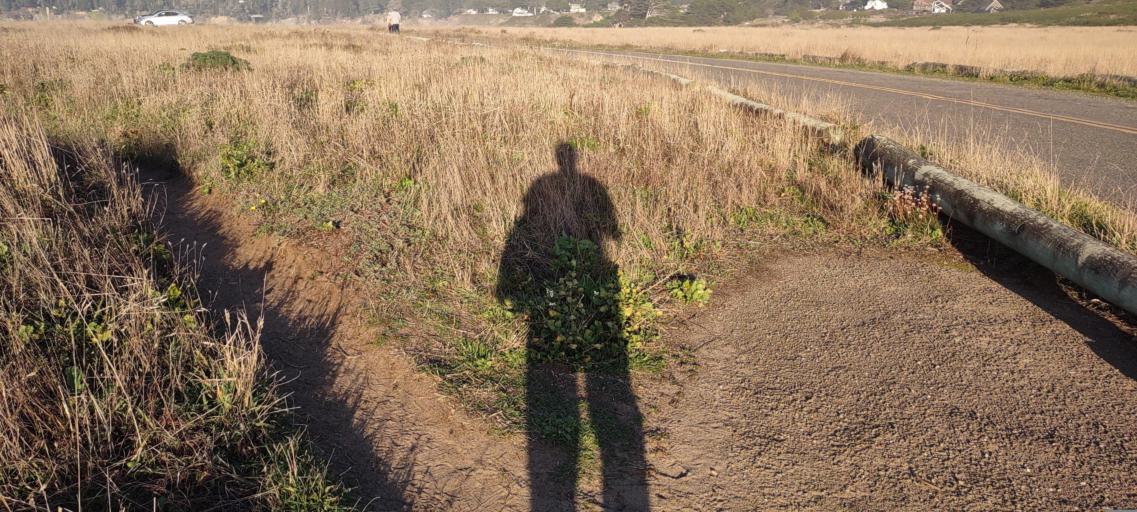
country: US
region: California
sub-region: Mendocino County
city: Fort Bragg
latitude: 39.3097
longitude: -123.8084
